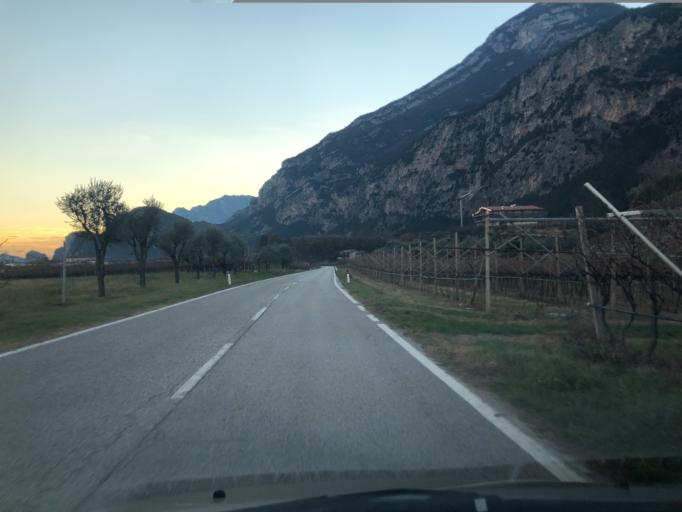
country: IT
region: Trentino-Alto Adige
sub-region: Provincia di Trento
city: Dro
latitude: 45.9678
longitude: 10.9164
